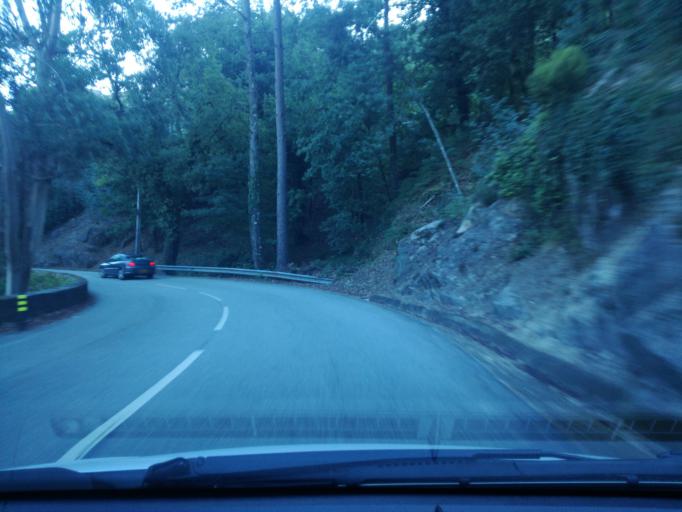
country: PT
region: Braga
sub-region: Vieira do Minho
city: Real
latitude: 41.6931
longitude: -8.1719
